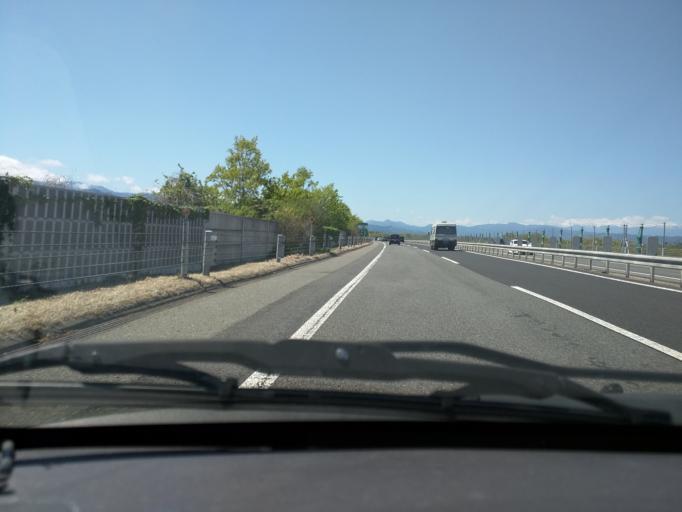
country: JP
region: Nagano
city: Suzaka
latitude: 36.7011
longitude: 138.3004
